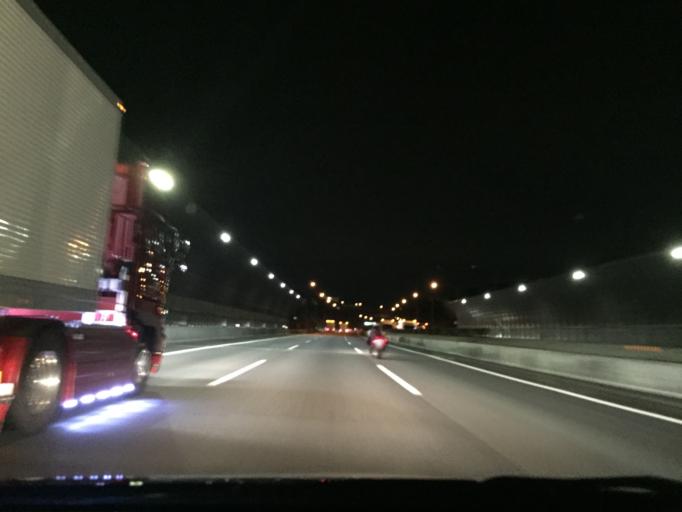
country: JP
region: Kanagawa
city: Hadano
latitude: 35.3672
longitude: 139.2600
